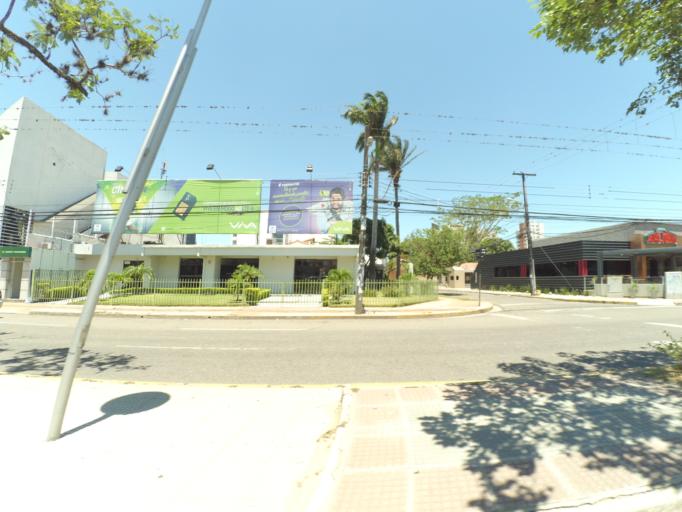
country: BO
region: Santa Cruz
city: Santa Cruz de la Sierra
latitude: -17.7671
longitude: -63.1942
